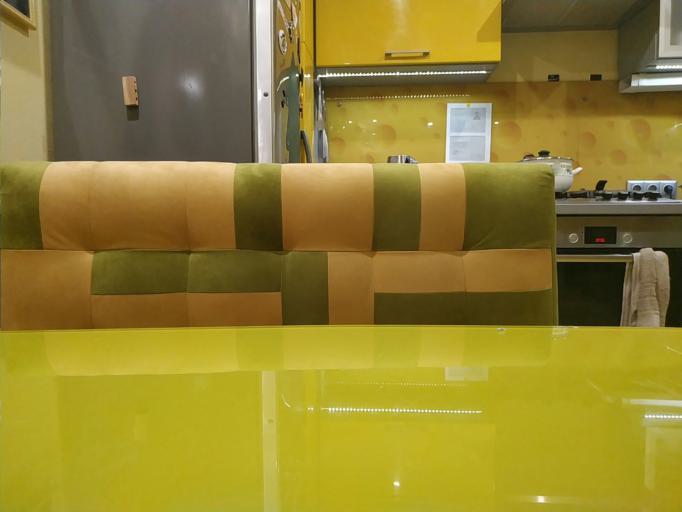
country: RU
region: Murmansk
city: Alakurtti
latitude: 66.1806
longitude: 30.2991
